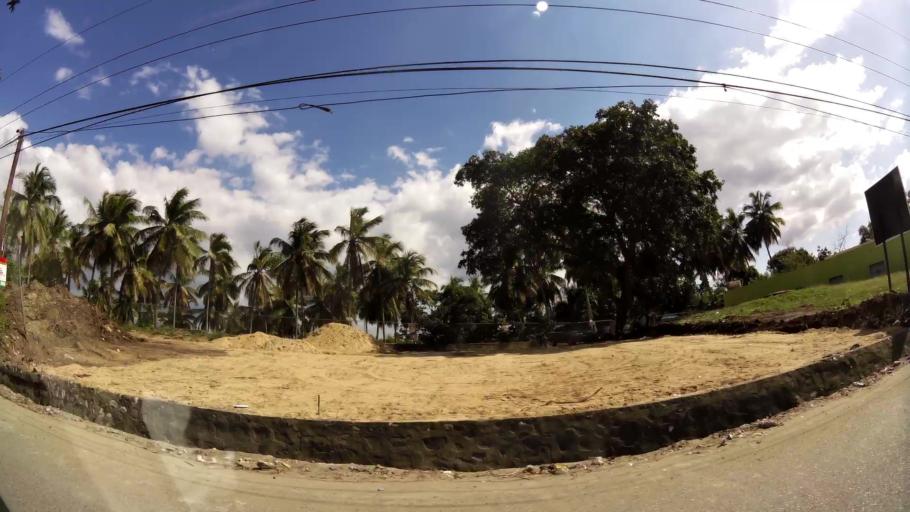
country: DO
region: San Cristobal
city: San Cristobal
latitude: 18.4249
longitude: -70.0694
